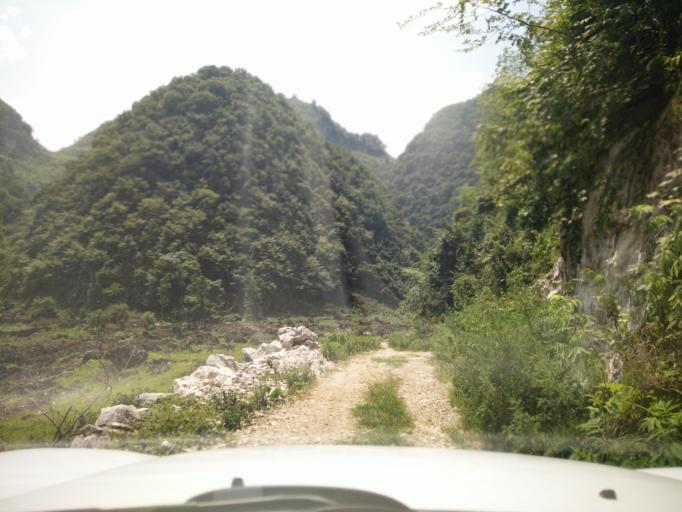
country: CN
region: Guangxi Zhuangzu Zizhiqu
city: Xinzhou
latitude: 25.0112
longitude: 105.7057
